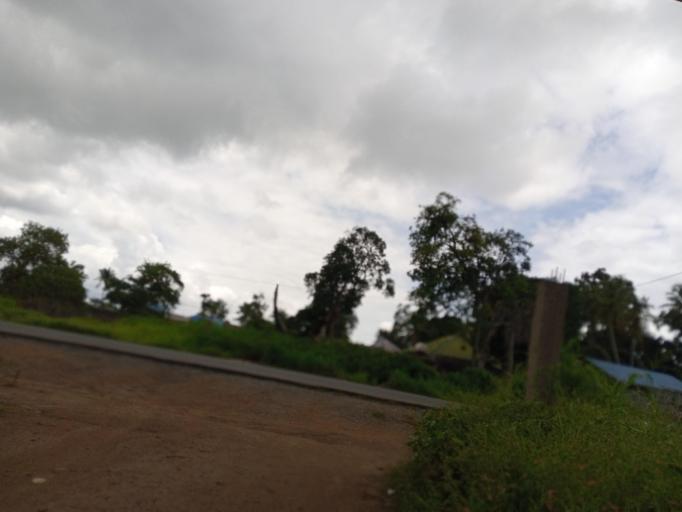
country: SL
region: Northern Province
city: Masoyila
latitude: 8.5770
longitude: -13.1635
